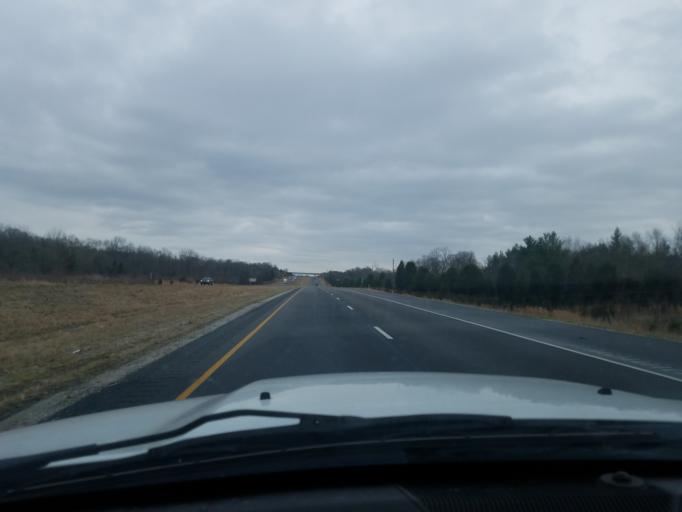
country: US
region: Indiana
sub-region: Crawford County
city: English
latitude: 38.2437
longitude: -86.4403
